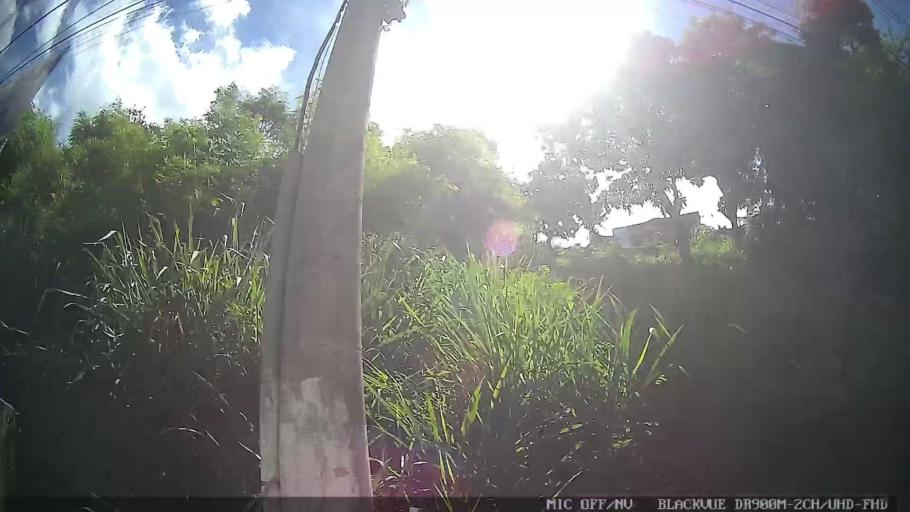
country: BR
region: Sao Paulo
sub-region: Pedreira
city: Pedreira
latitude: -22.7449
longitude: -46.9042
